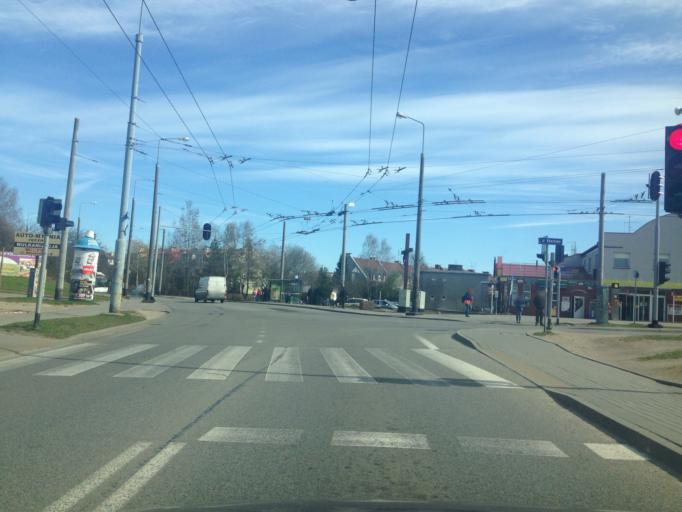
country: PL
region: Pomeranian Voivodeship
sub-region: Gdynia
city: Wielki Kack
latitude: 54.4741
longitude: 18.4651
